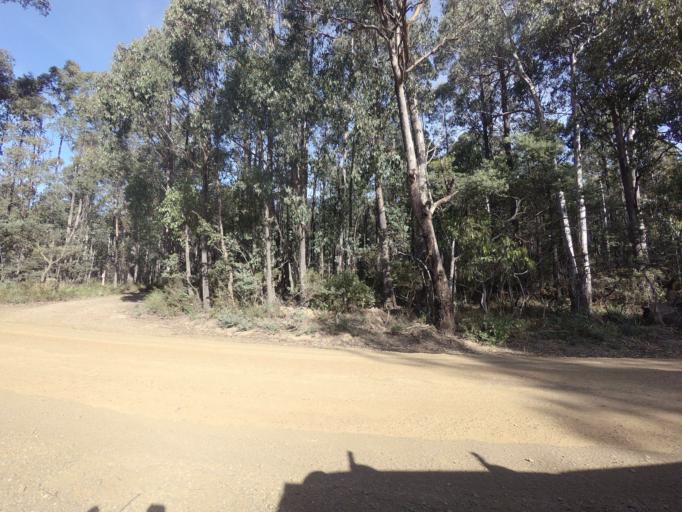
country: AU
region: Tasmania
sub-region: Sorell
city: Sorell
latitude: -42.4897
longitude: 147.5160
